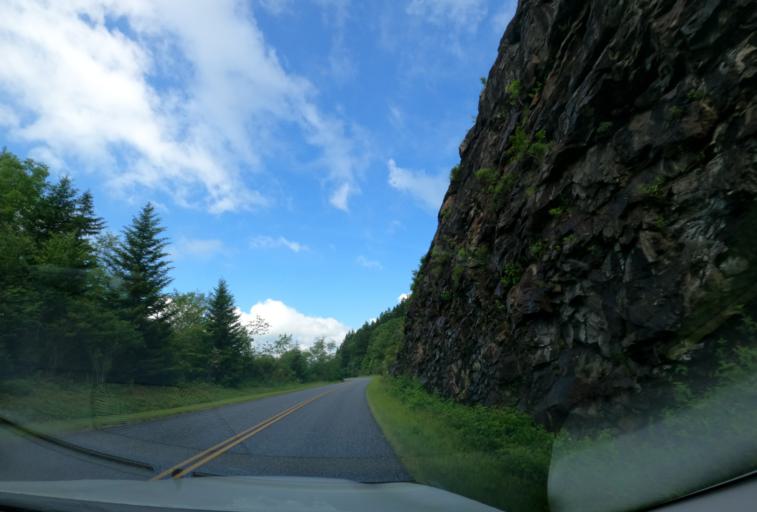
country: US
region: North Carolina
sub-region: Haywood County
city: Hazelwood
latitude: 35.3726
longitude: -82.9998
